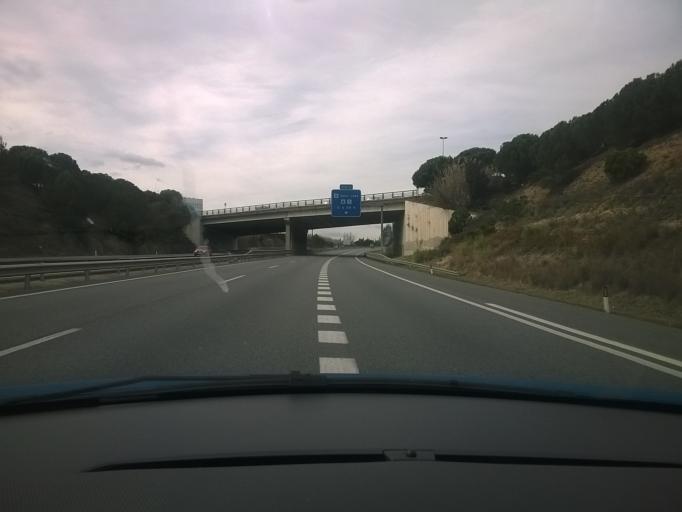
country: ES
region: Catalonia
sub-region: Provincia de Barcelona
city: Rubi
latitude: 41.4916
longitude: 2.0550
